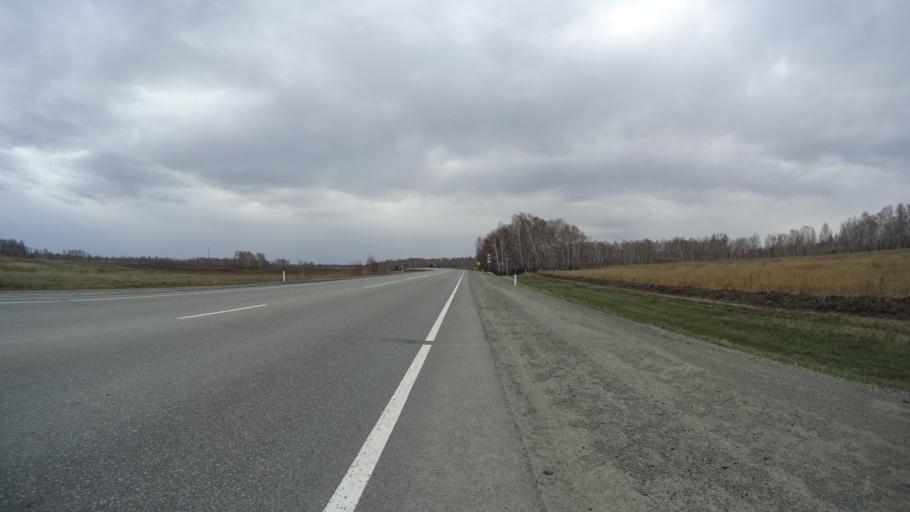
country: RU
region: Chelyabinsk
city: Yemanzhelinsk
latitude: 54.6990
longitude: 61.2514
